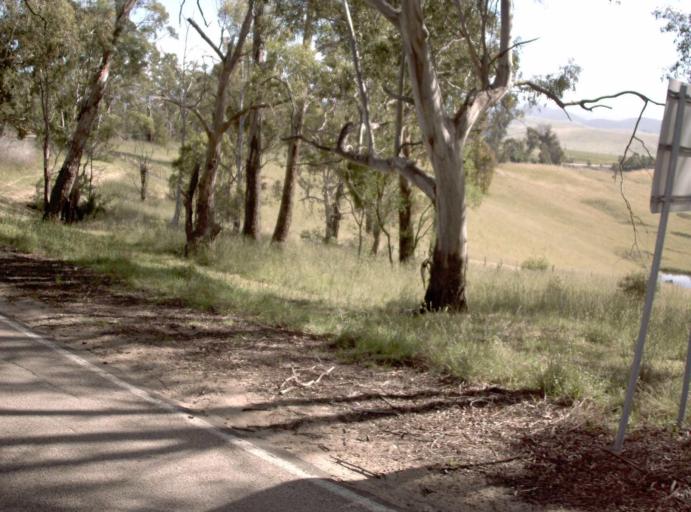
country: AU
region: Victoria
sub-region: East Gippsland
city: Lakes Entrance
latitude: -37.5193
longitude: 148.1620
